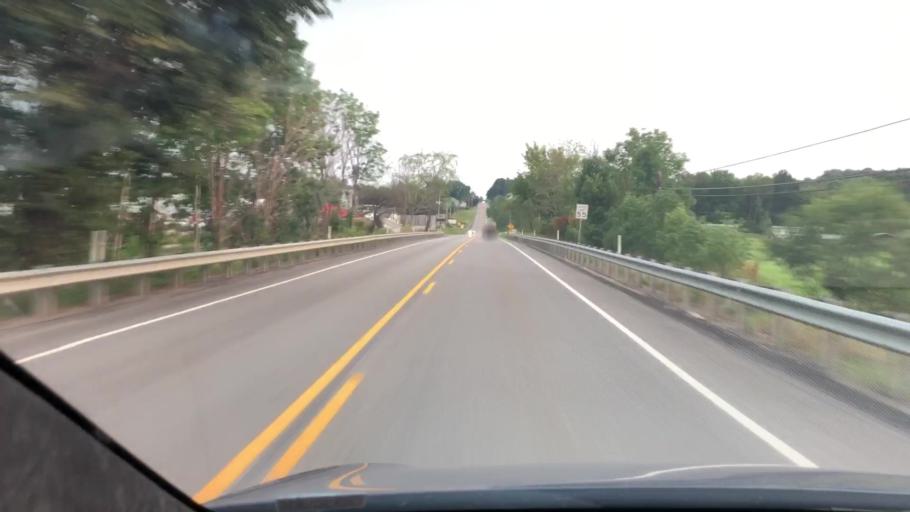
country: US
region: Pennsylvania
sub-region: Butler County
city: Slippery Rock
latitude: 41.1220
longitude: -80.0080
